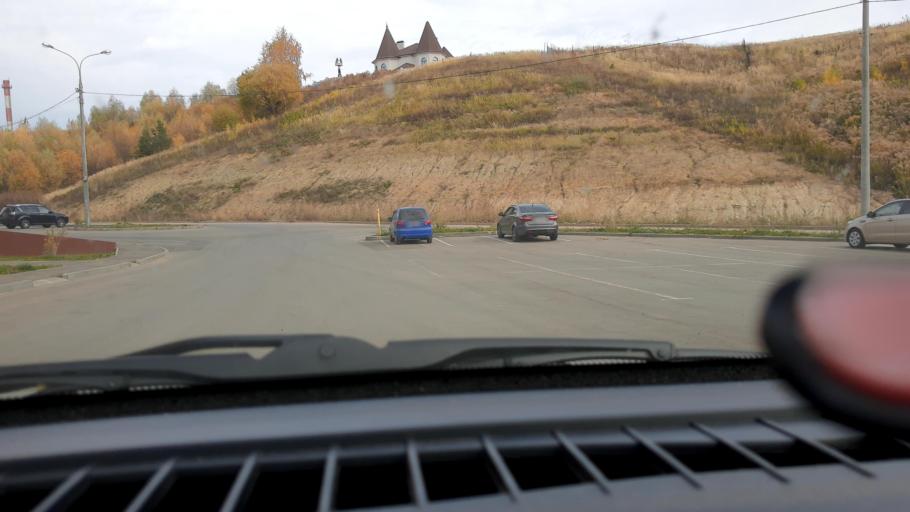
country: RU
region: Nizjnij Novgorod
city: Afonino
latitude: 56.2799
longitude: 44.0910
